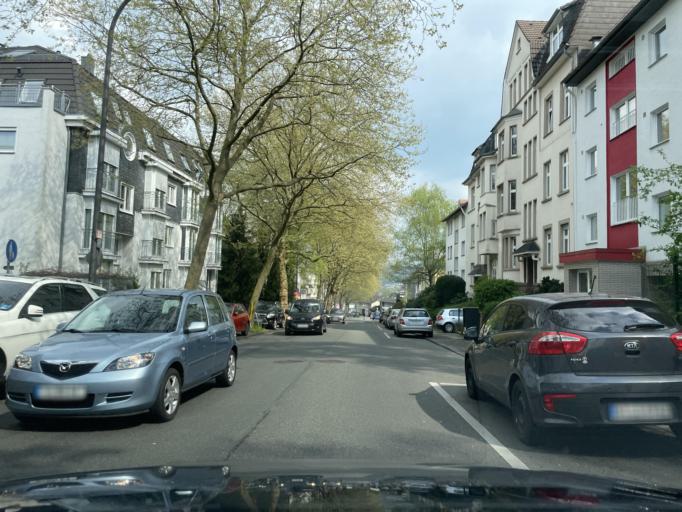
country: DE
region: North Rhine-Westphalia
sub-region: Regierungsbezirk Dusseldorf
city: Wuppertal
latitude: 51.2663
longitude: 7.2161
